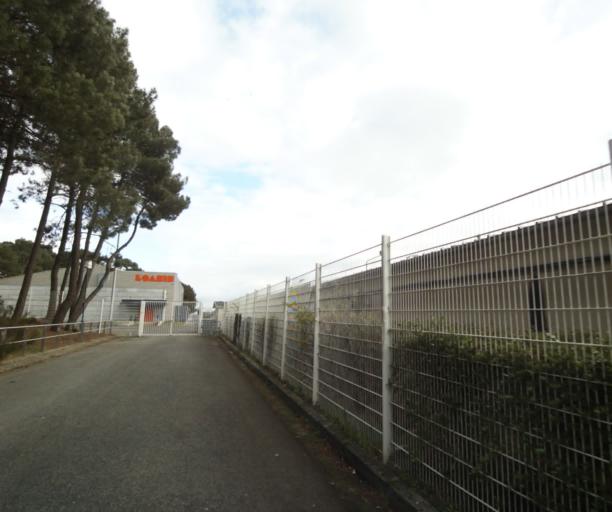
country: FR
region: Pays de la Loire
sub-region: Departement de la Sarthe
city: Arnage
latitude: 47.9598
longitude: 0.2012
